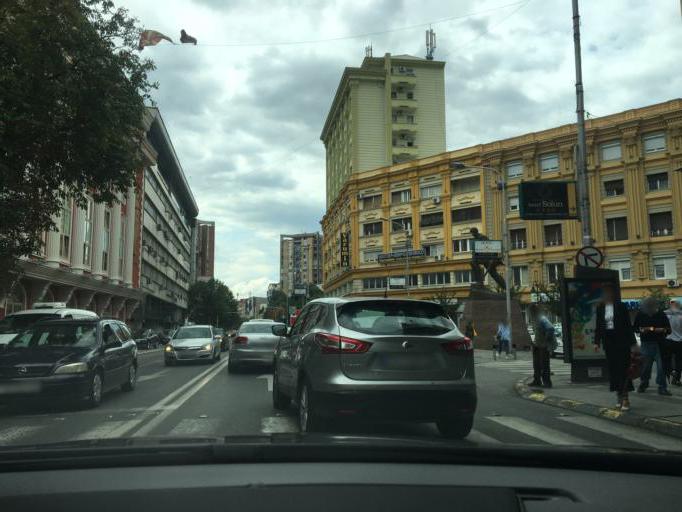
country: MK
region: Karpos
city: Skopje
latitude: 41.9948
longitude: 21.4298
